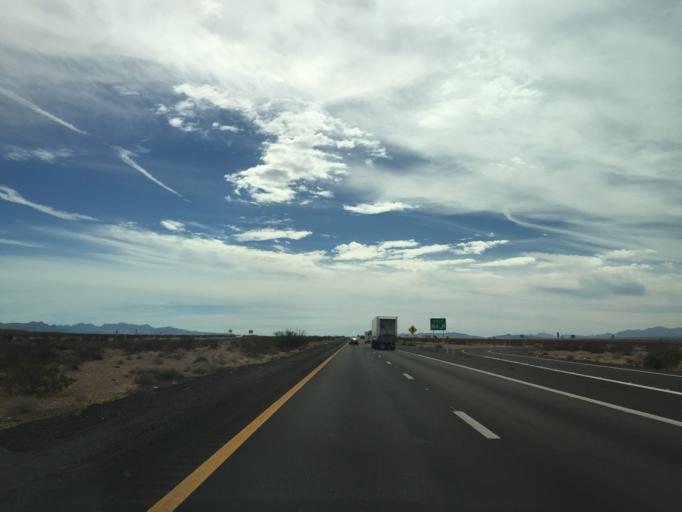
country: US
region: Nevada
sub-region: Clark County
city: Moapa Town
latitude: 36.5905
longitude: -114.6479
